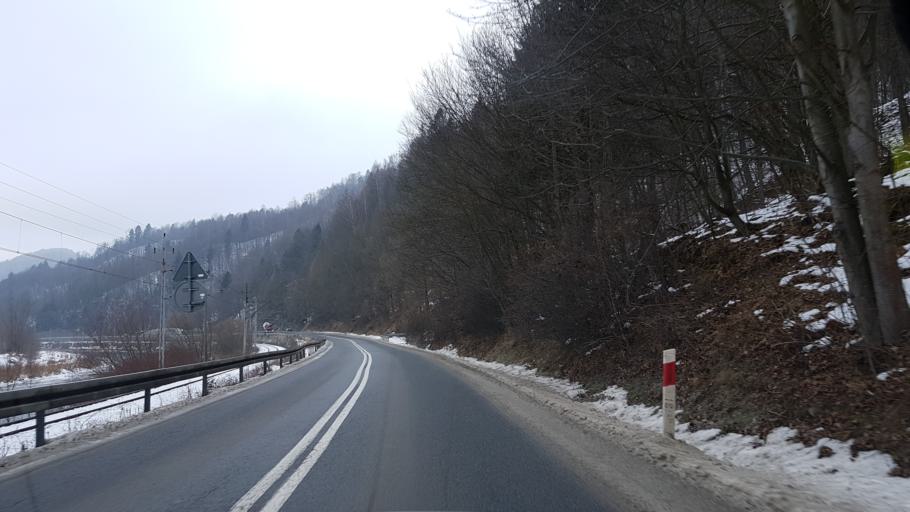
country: PL
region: Lesser Poland Voivodeship
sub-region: Powiat nowosadecki
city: Piwniczna-Zdroj
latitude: 49.4161
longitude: 20.7426
